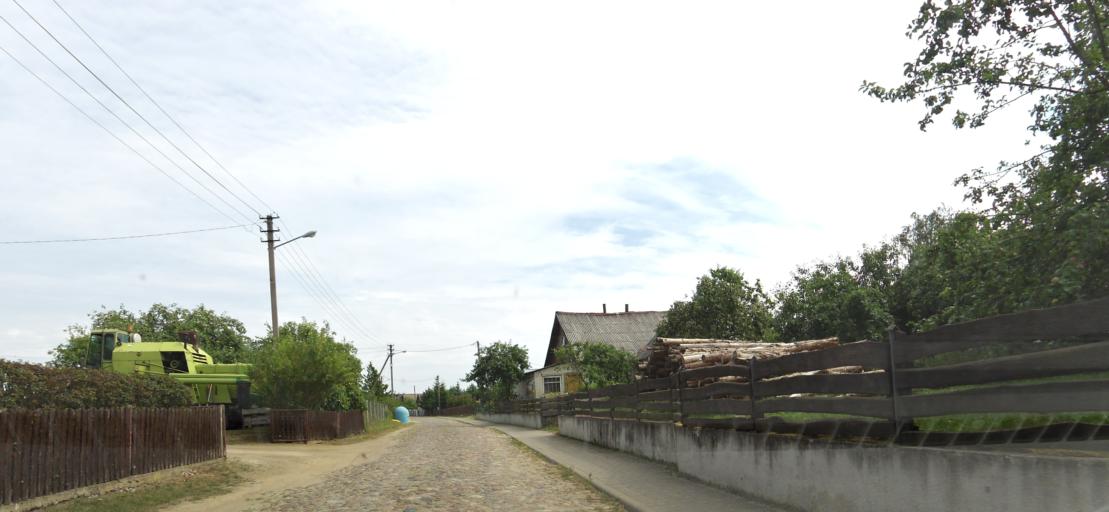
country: LT
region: Vilnius County
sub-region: Trakai
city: Rudiskes
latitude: 54.3534
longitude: 24.8328
